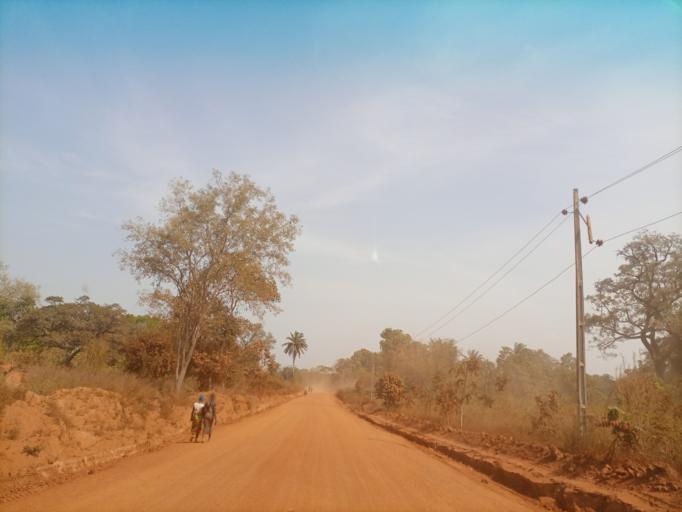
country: NG
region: Enugu
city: Eha Amufu
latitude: 6.6683
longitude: 7.7478
